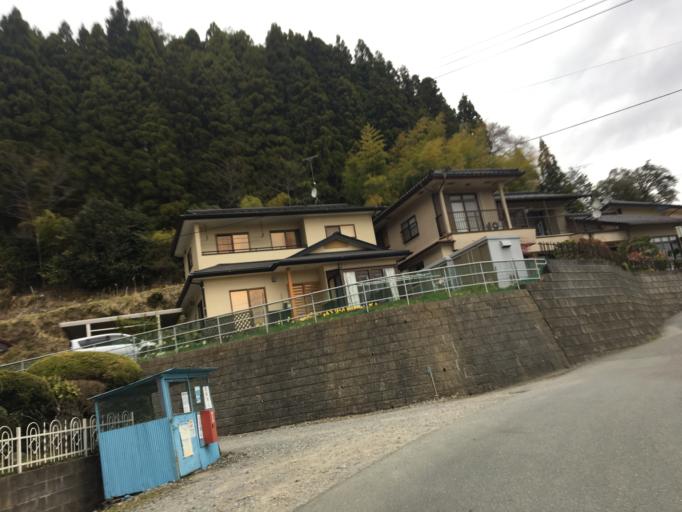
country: JP
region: Iwate
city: Ofunato
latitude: 38.9140
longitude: 141.5778
